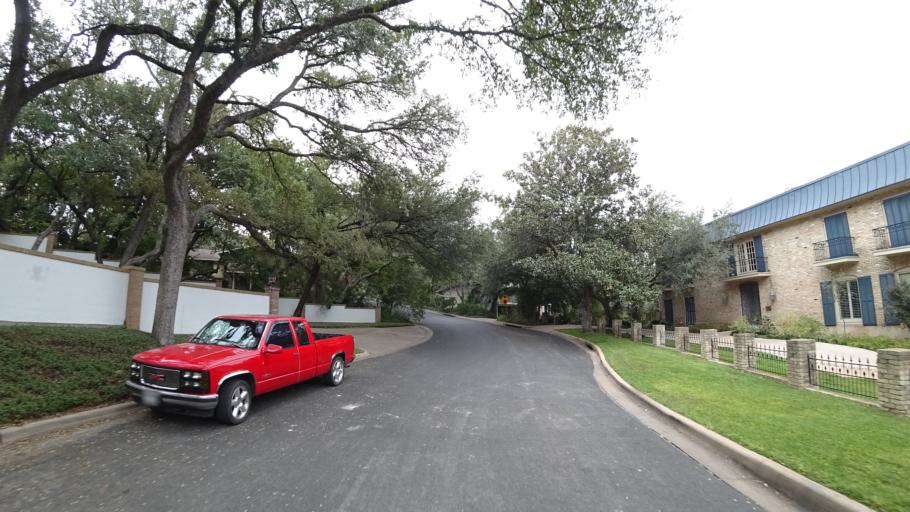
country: US
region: Texas
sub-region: Travis County
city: West Lake Hills
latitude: 30.3102
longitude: -97.7724
